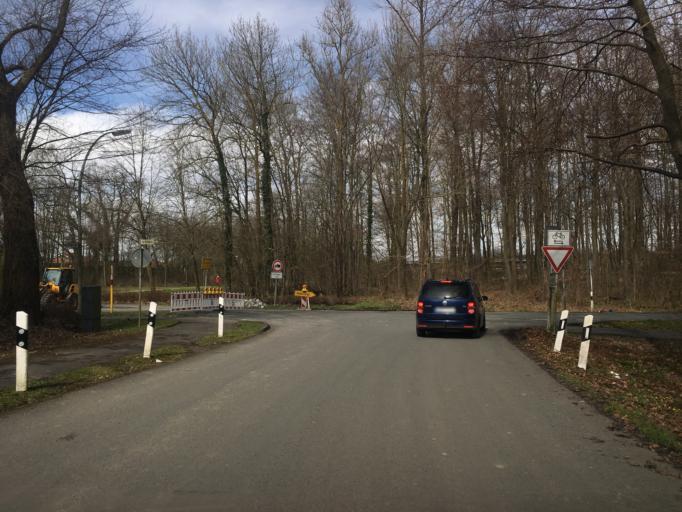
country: DE
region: North Rhine-Westphalia
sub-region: Regierungsbezirk Munster
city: Nordkirchen
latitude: 51.7359
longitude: 7.5326
